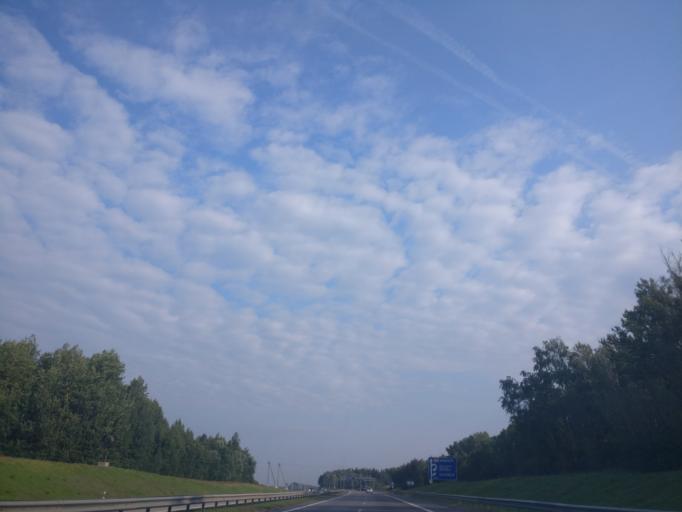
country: BY
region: Minsk
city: Lahoysk
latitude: 54.1698
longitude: 27.8192
